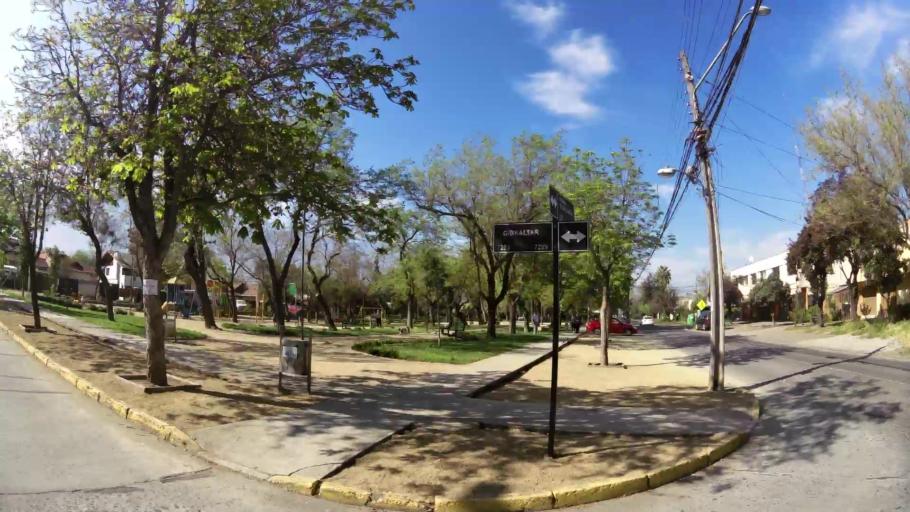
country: CL
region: Santiago Metropolitan
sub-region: Provincia de Santiago
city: Villa Presidente Frei, Nunoa, Santiago, Chile
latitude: -33.4484
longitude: -70.5560
